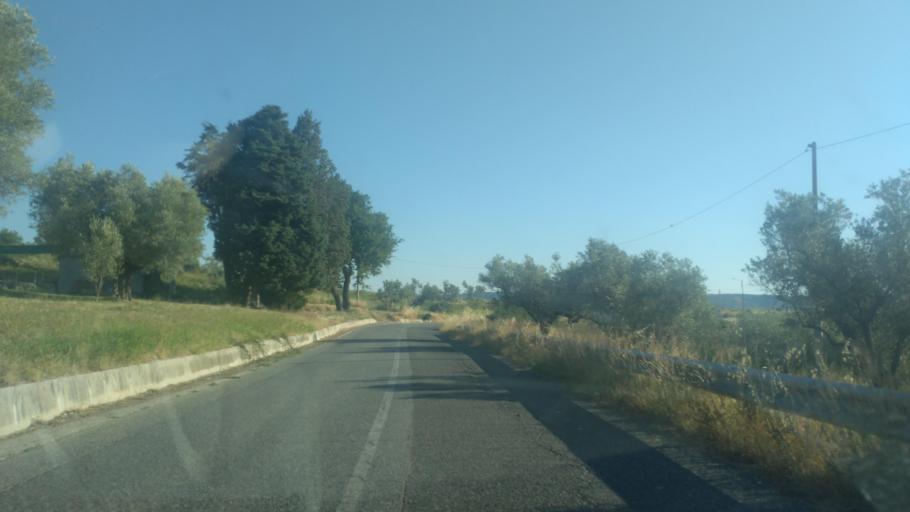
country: IT
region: Calabria
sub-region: Provincia di Catanzaro
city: Squillace
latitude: 38.7776
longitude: 16.5018
